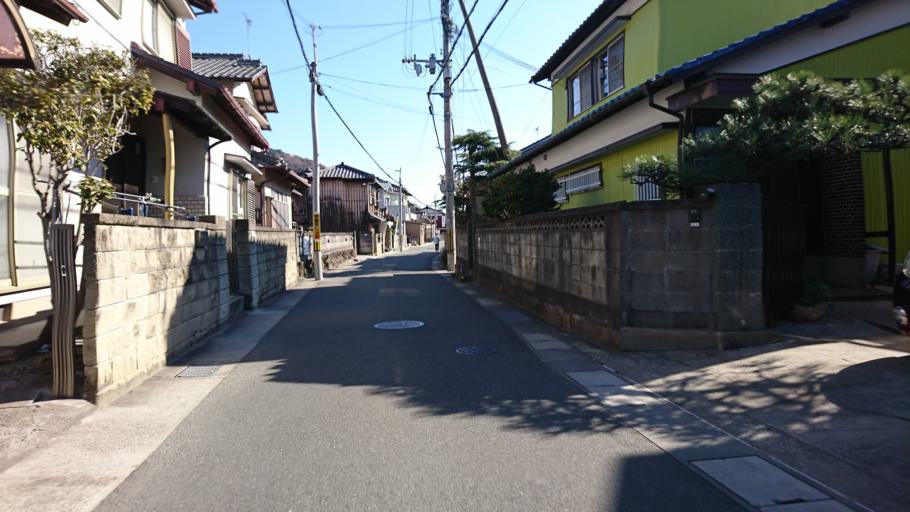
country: JP
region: Hyogo
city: Kakogawacho-honmachi
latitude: 34.7931
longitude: 134.7915
